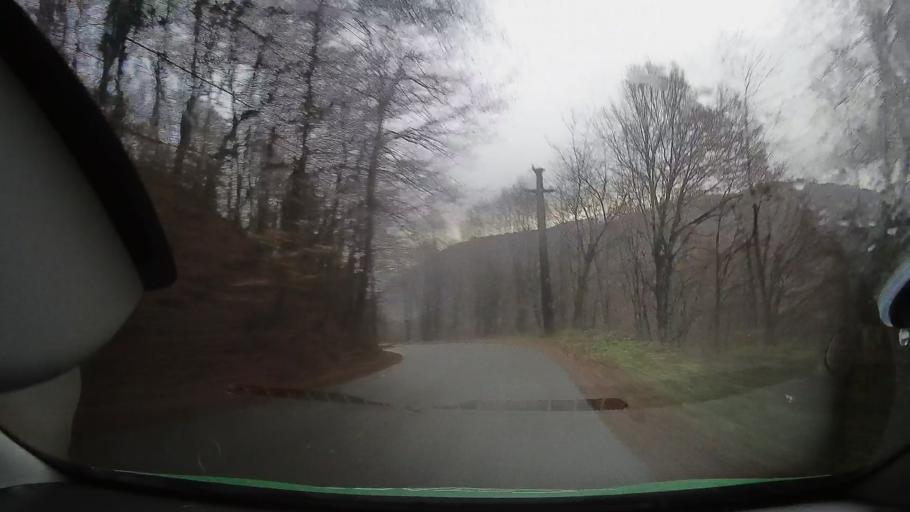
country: RO
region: Hunedoara
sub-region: Comuna Ribita
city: Ribita
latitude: 46.2506
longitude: 22.7487
